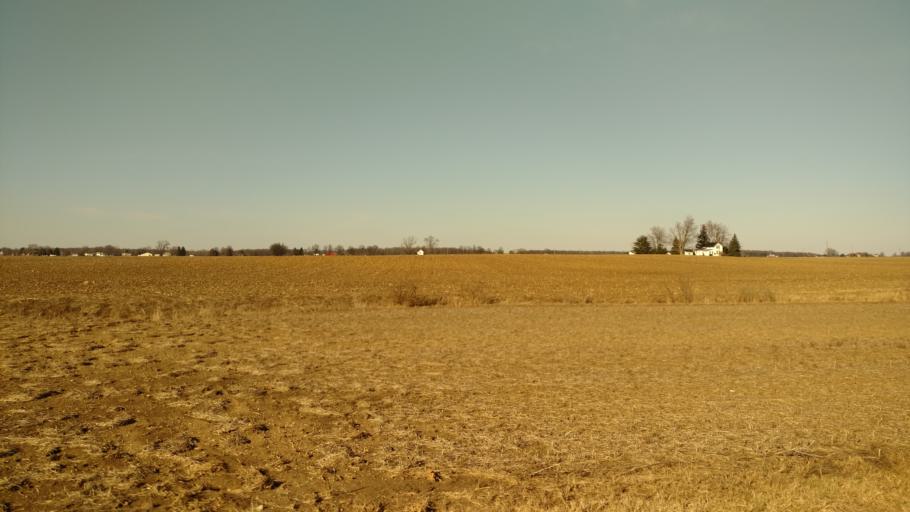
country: US
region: Ohio
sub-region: Crawford County
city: Bucyrus
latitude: 40.7045
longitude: -82.9131
